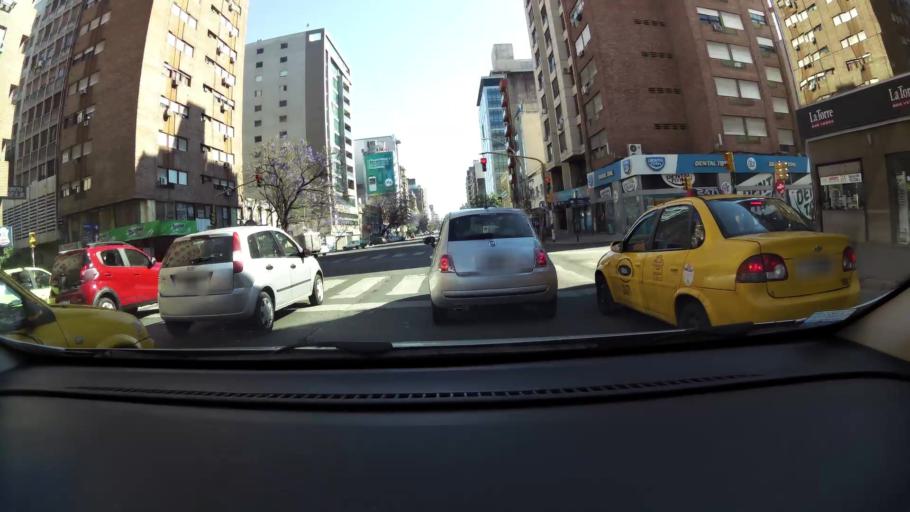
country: AR
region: Cordoba
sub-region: Departamento de Capital
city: Cordoba
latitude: -31.4171
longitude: -64.1801
